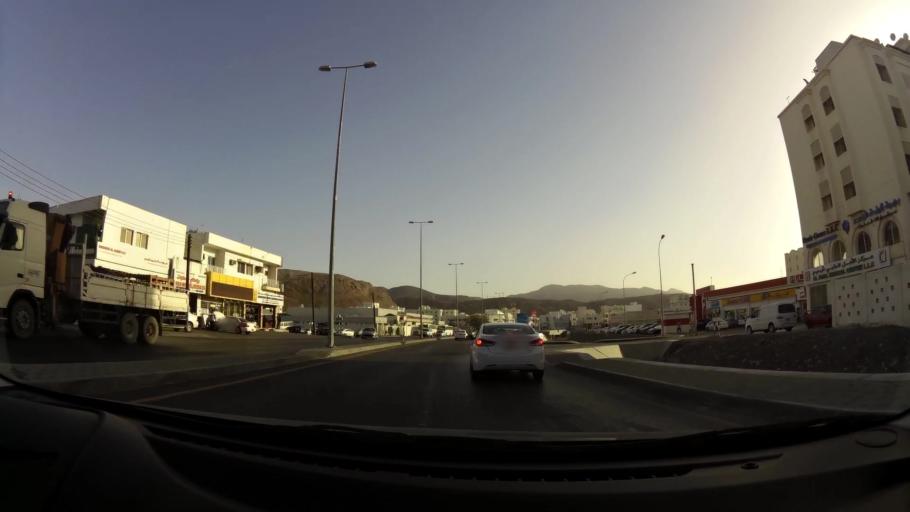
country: OM
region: Muhafazat Masqat
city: Muscat
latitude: 23.5899
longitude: 58.5540
